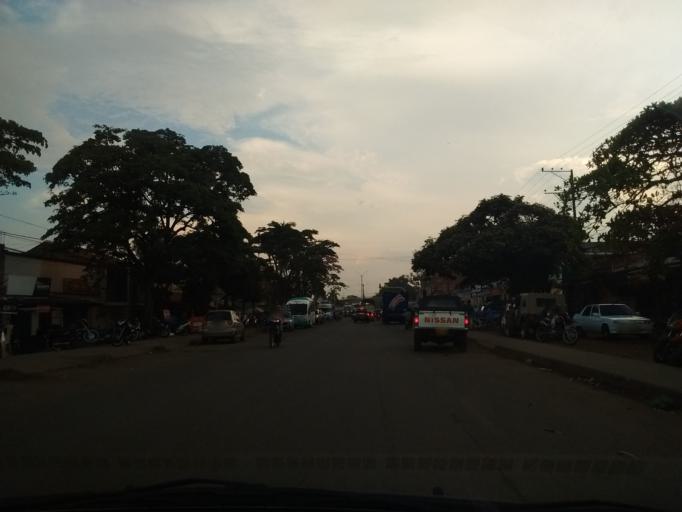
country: CO
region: Cauca
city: Santander de Quilichao
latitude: 3.0059
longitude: -76.4872
